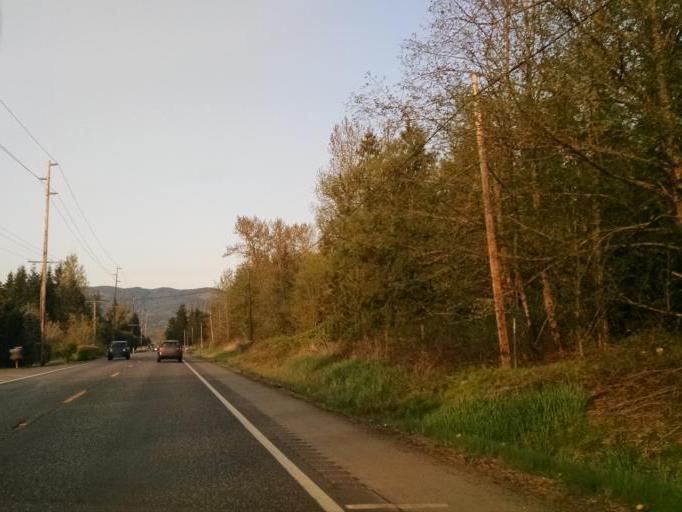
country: US
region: Washington
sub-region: Whatcom County
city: Sudden Valley
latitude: 48.8206
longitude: -122.3233
